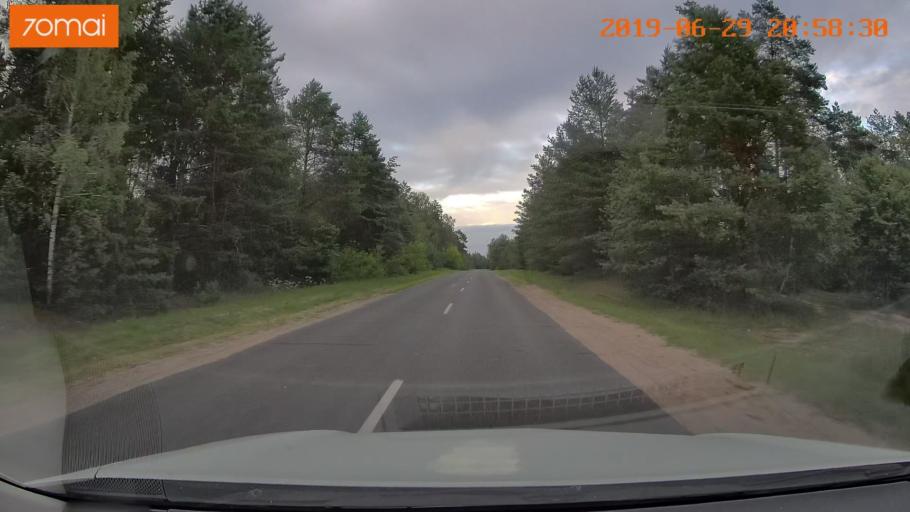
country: BY
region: Brest
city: Hantsavichy
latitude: 52.7303
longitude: 26.3873
